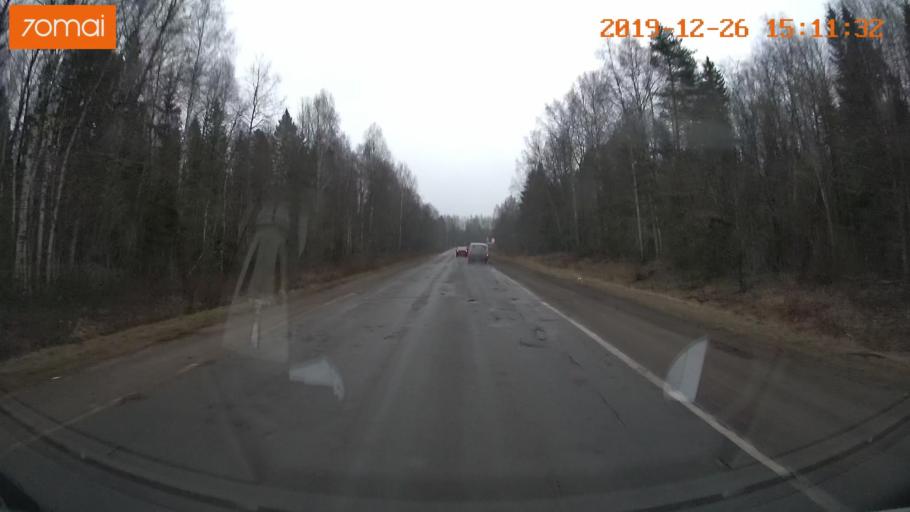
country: RU
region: Jaroslavl
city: Rybinsk
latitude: 58.1340
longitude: 38.8632
